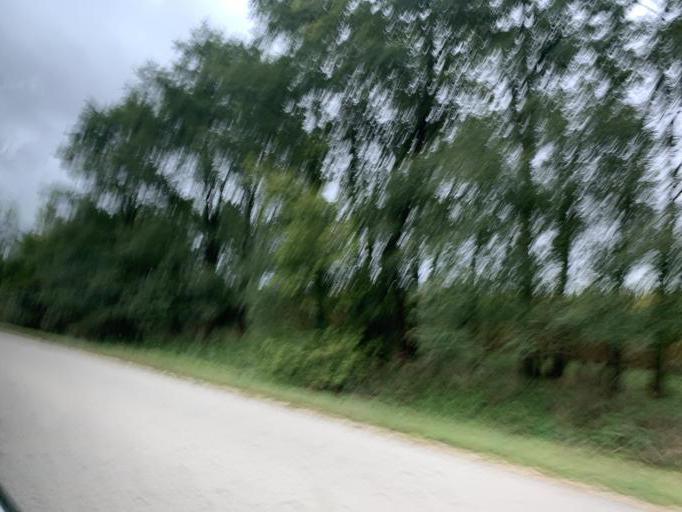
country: US
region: Wisconsin
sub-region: Sauk County
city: Prairie du Sac
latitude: 43.3018
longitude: -89.7789
